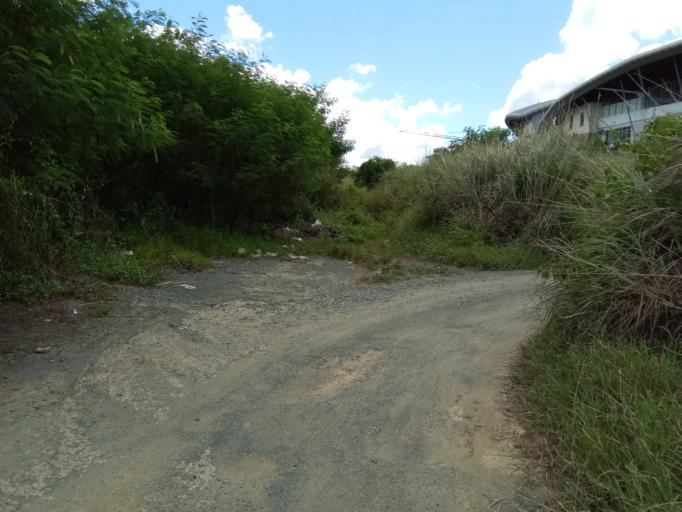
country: PH
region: Calabarzon
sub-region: Province of Cavite
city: Manggahan
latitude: 14.2915
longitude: 120.9165
